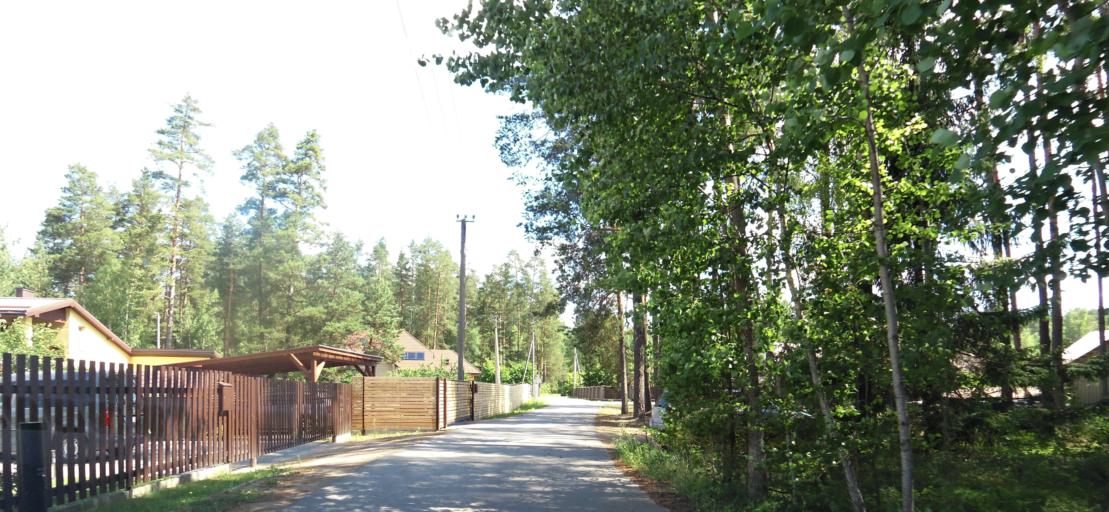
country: LT
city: Nemencine
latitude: 54.8251
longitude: 25.4121
